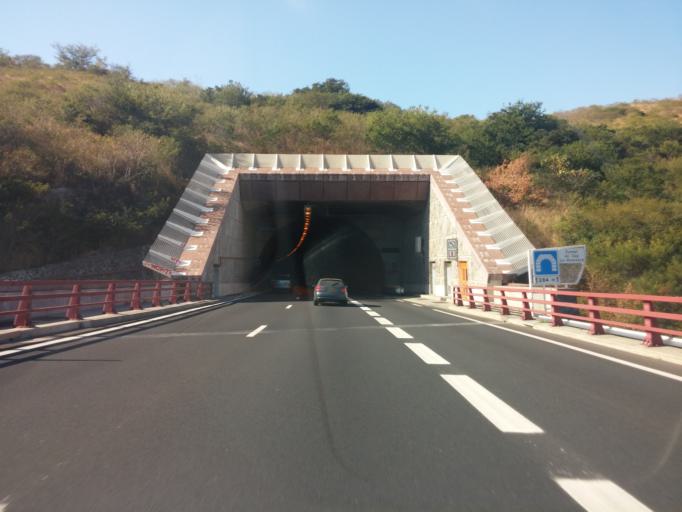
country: RE
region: Reunion
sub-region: Reunion
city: Saint-Paul
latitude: -21.0311
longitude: 55.2534
